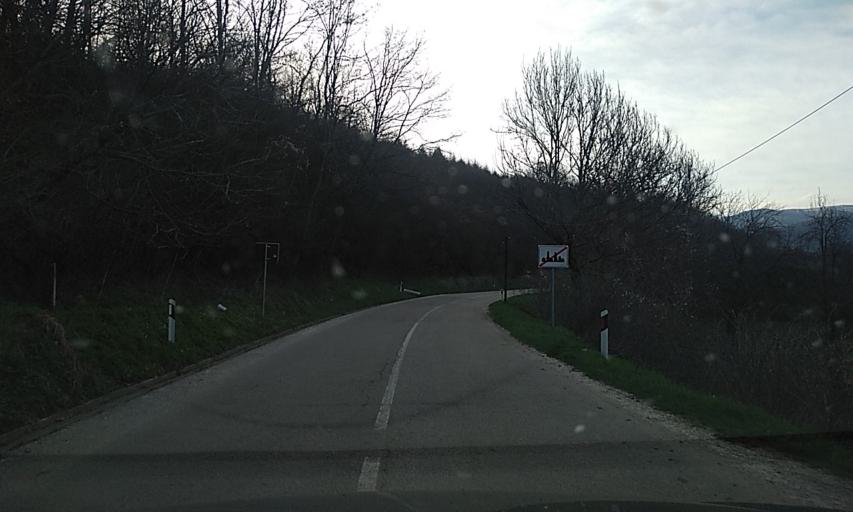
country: RS
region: Central Serbia
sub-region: Pcinjski Okrug
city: Bosilegrad
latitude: 42.4687
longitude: 22.4832
